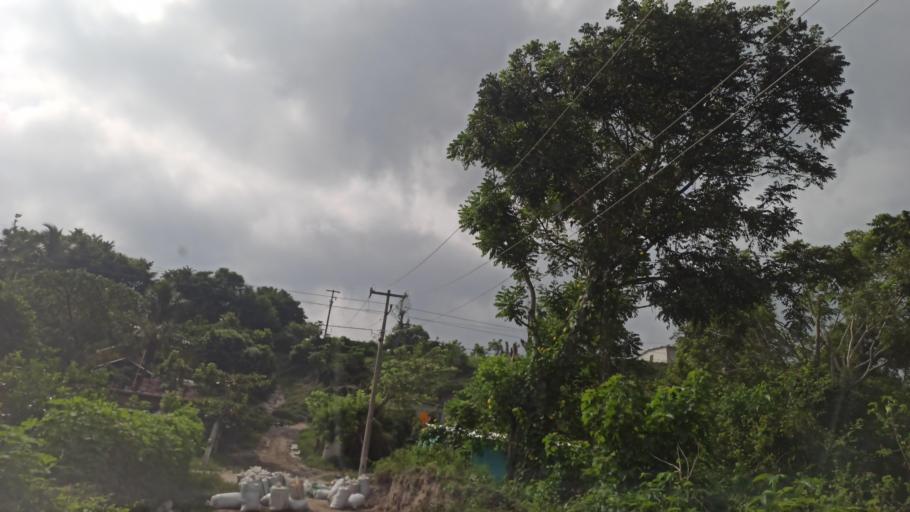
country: MX
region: Puebla
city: San Jose Acateno
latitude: 20.1610
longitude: -97.1828
